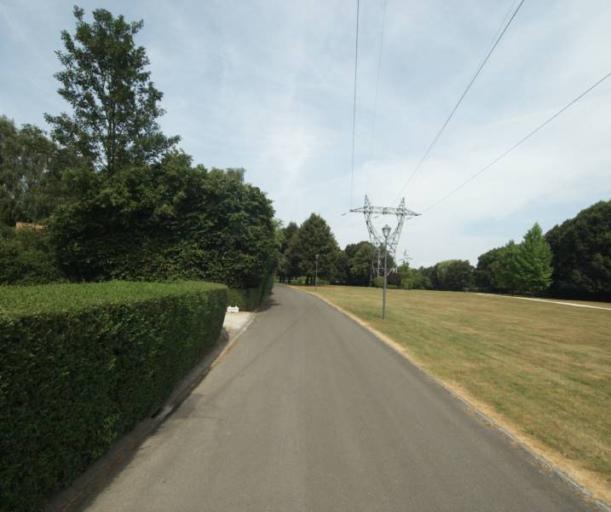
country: FR
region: Nord-Pas-de-Calais
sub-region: Departement du Nord
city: Mouvaux
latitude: 50.7192
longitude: 3.1208
